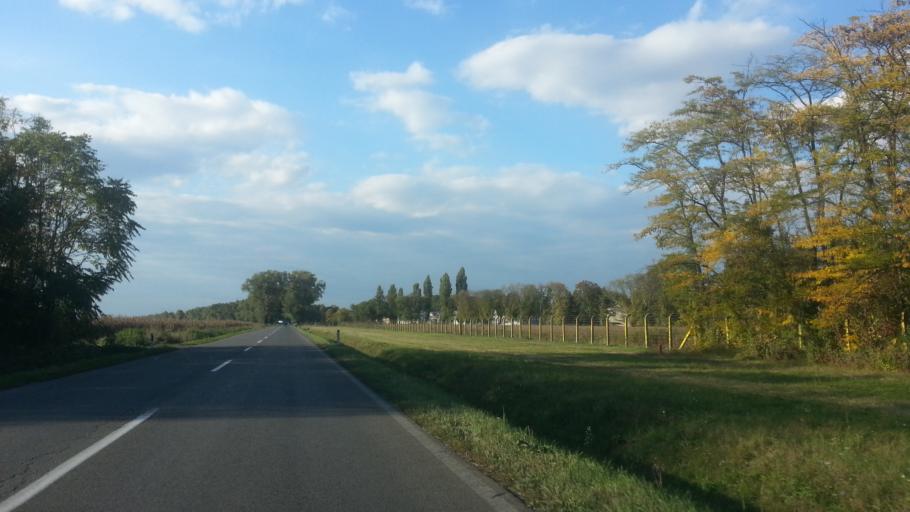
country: RS
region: Autonomna Pokrajina Vojvodina
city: Nova Pazova
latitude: 44.9206
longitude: 20.2510
